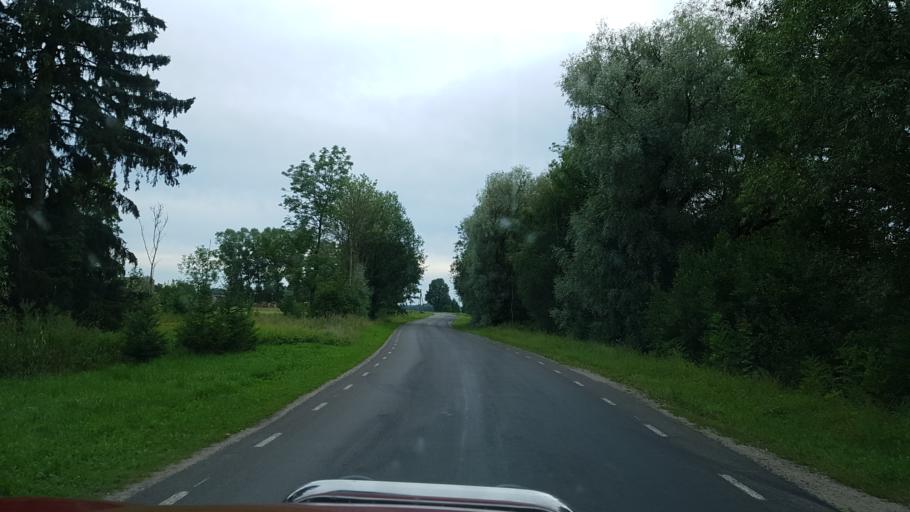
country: EE
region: Laeaene
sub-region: Lihula vald
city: Lihula
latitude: 58.8541
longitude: 23.7990
